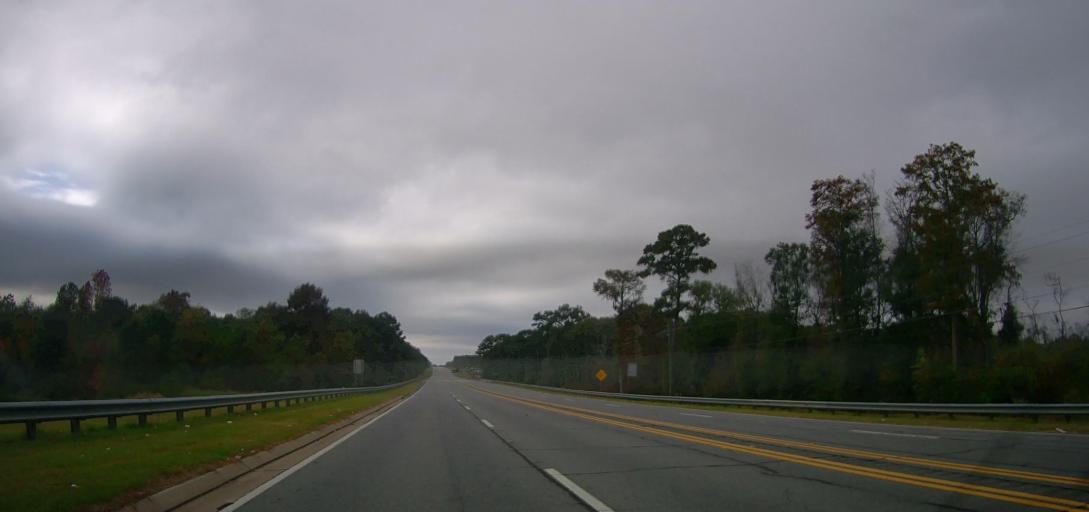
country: US
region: Georgia
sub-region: Tift County
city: Omega
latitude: 31.2985
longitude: -83.6557
